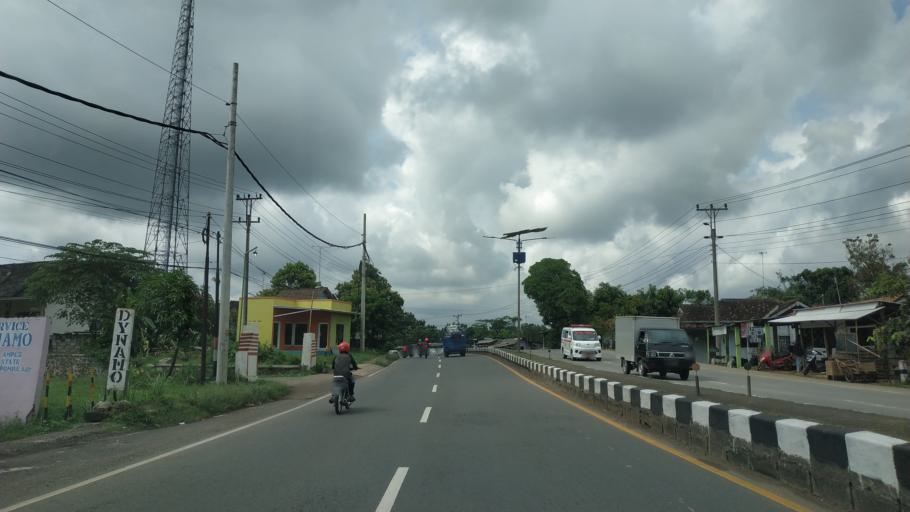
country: ID
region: Central Java
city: Pekalongan
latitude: -6.9455
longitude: 109.7773
